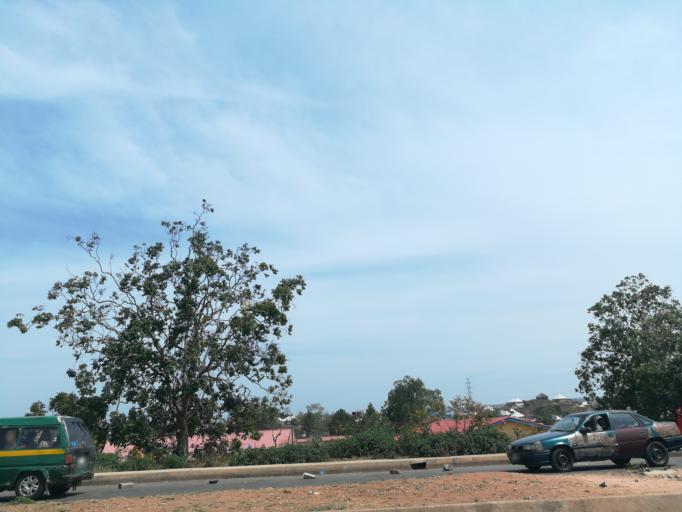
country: NG
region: Plateau
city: Bukuru
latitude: 9.8395
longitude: 8.8658
